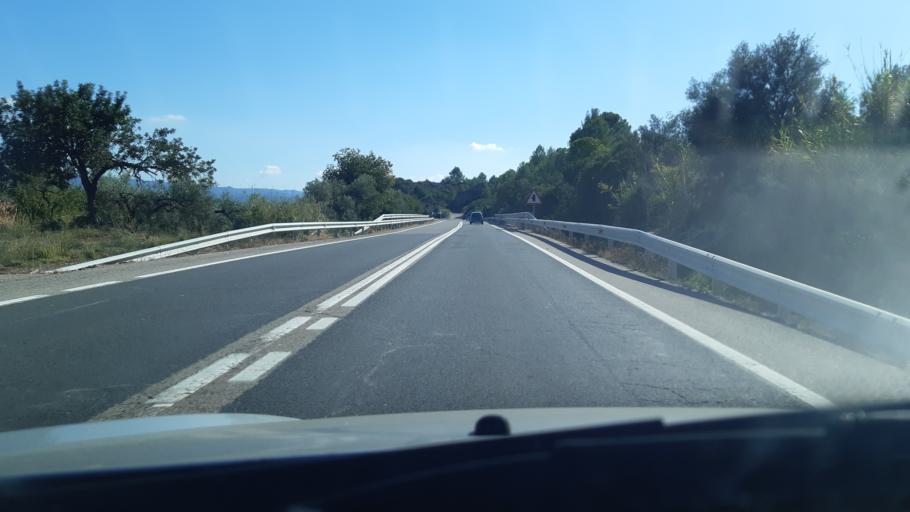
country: ES
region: Catalonia
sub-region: Provincia de Tarragona
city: Tivenys
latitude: 40.9006
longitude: 0.4835
